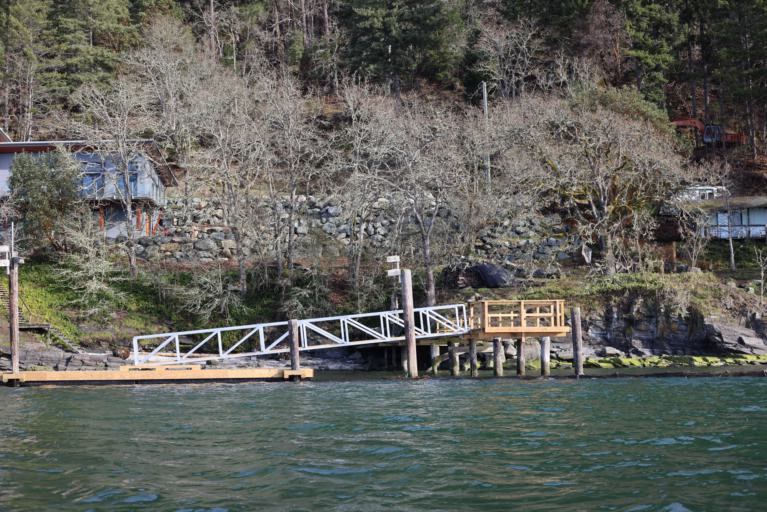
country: CA
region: British Columbia
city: Duncan
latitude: 48.7615
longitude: -123.6157
